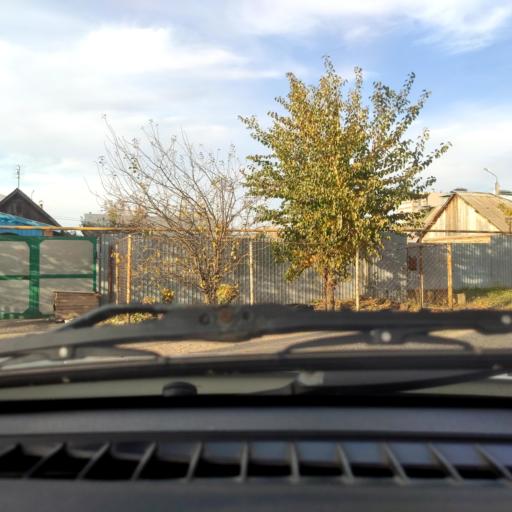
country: RU
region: Samara
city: Tol'yatti
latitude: 53.5256
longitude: 49.4101
